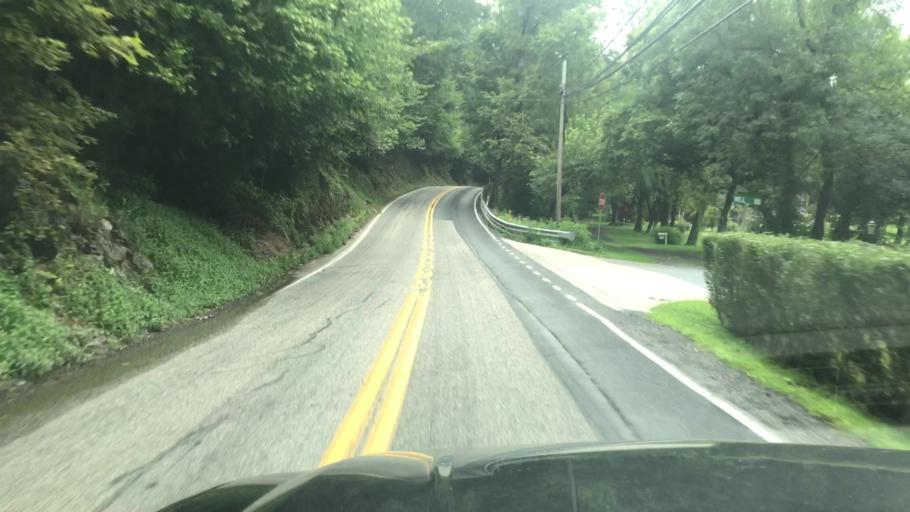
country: US
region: Pennsylvania
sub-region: Cumberland County
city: Shiremanstown
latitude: 40.2633
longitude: -76.9777
